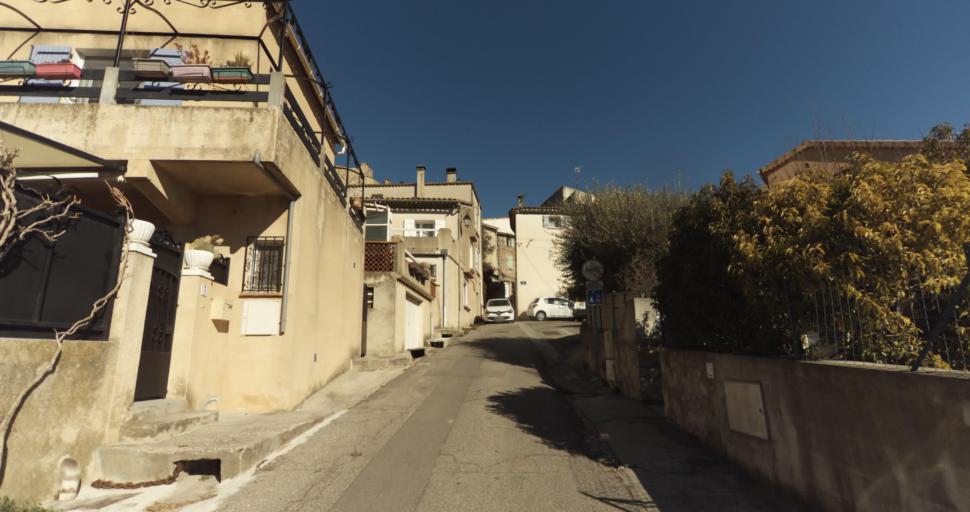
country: FR
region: Provence-Alpes-Cote d'Azur
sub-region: Departement des Bouches-du-Rhone
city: Peypin
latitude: 43.3862
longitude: 5.5787
